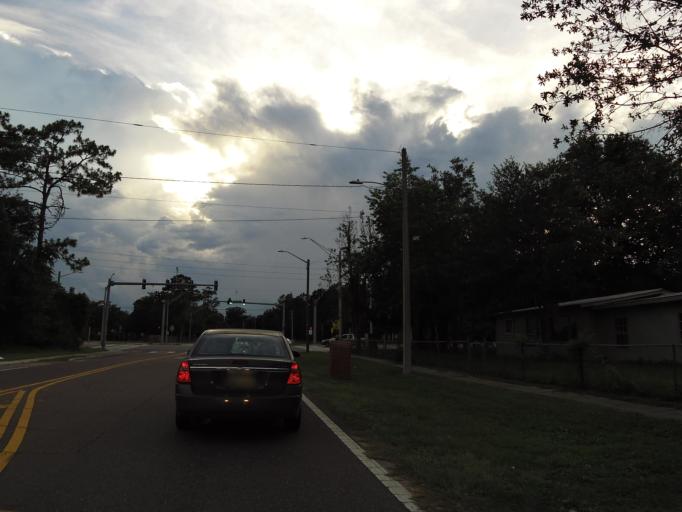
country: US
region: Florida
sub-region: Clay County
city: Bellair-Meadowbrook Terrace
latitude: 30.3021
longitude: -81.7973
